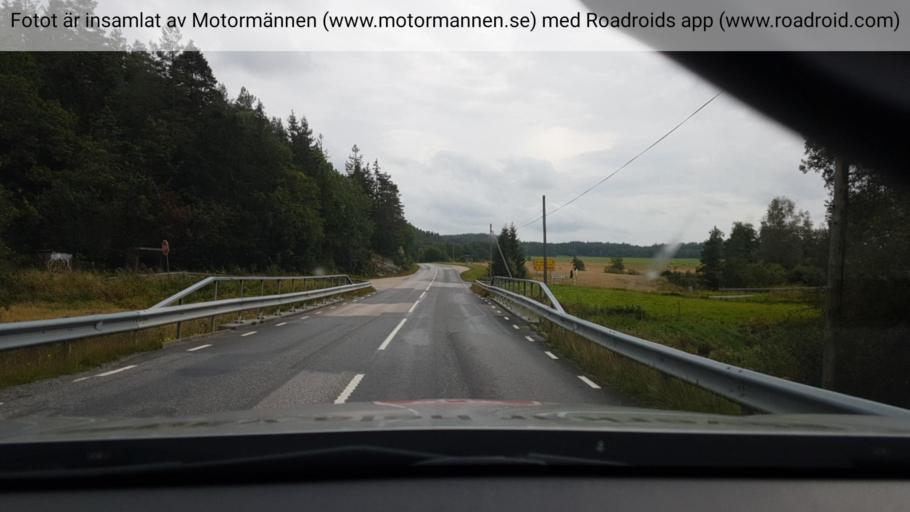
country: SE
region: Vaestra Goetaland
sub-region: Sotenas Kommun
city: Hunnebostrand
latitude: 58.5586
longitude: 11.4018
